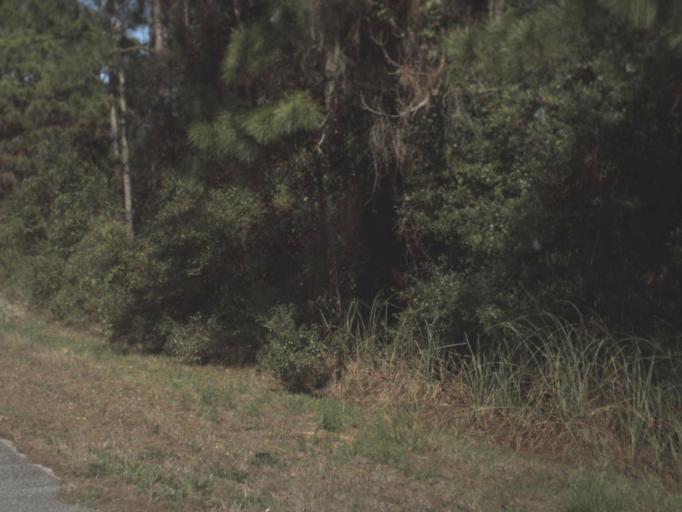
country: US
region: Florida
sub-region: Wakulla County
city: Crawfordville
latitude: 29.9527
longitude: -84.3854
